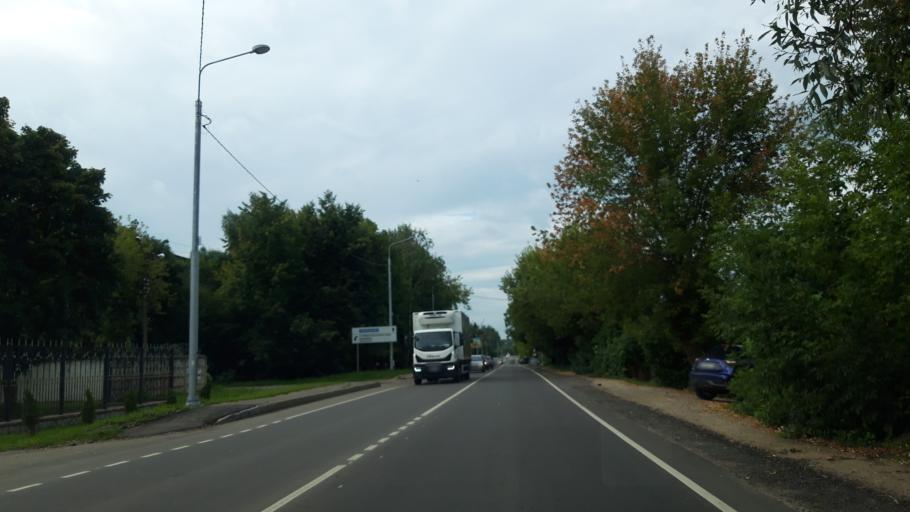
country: RU
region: Moskovskaya
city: Solnechnogorsk
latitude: 56.1973
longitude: 36.9670
